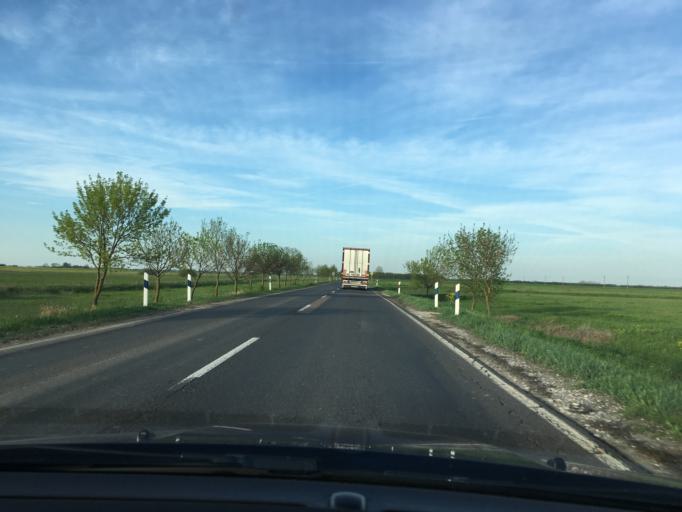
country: HU
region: Hajdu-Bihar
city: Berettyoujfalu
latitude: 47.1532
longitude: 21.4976
